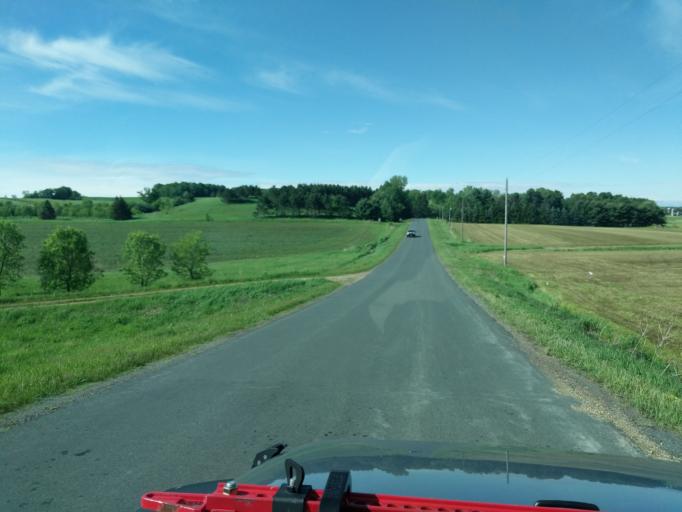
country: US
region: Wisconsin
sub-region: Pierce County
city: River Falls
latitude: 44.8691
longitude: -92.5132
